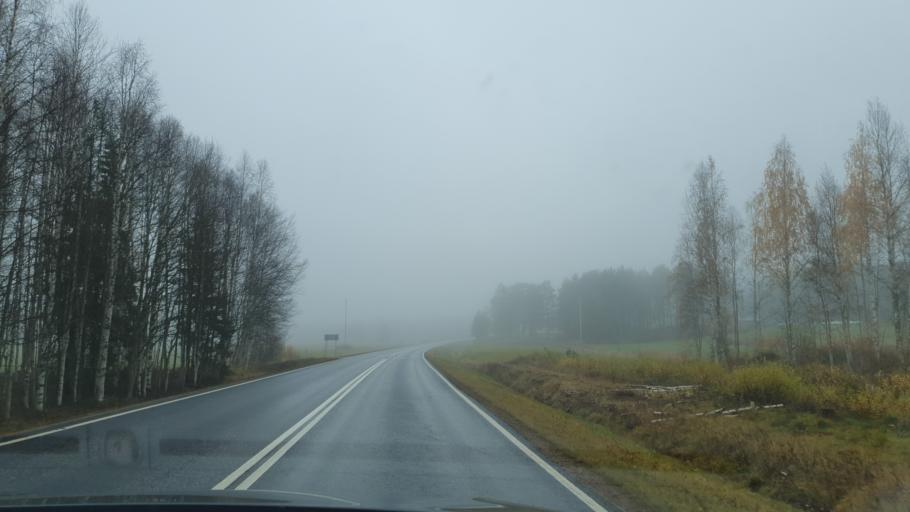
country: FI
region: Lapland
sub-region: Rovaniemi
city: Rovaniemi
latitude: 66.8084
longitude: 25.4100
